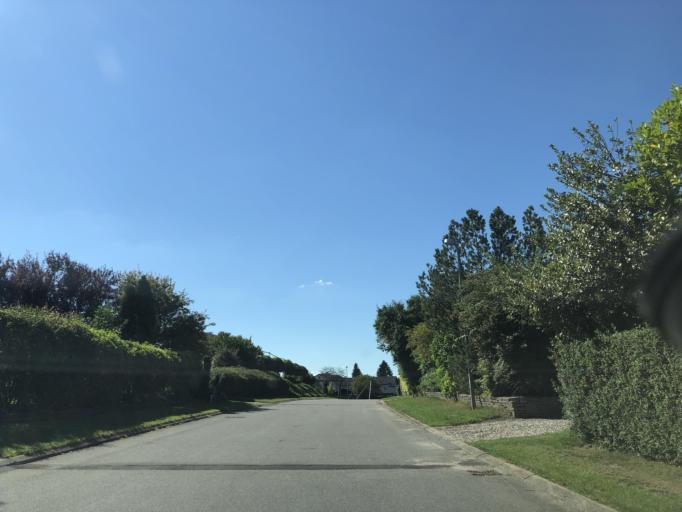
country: DK
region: North Denmark
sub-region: Mariagerfjord Kommune
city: Hobro
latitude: 56.6590
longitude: 9.7777
